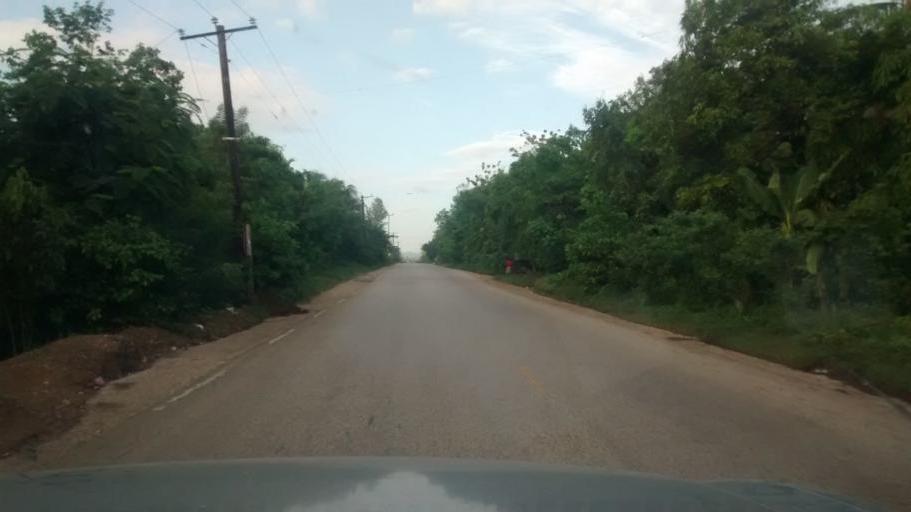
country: HT
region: Nippes
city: Miragoane
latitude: 18.4245
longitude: -72.9928
